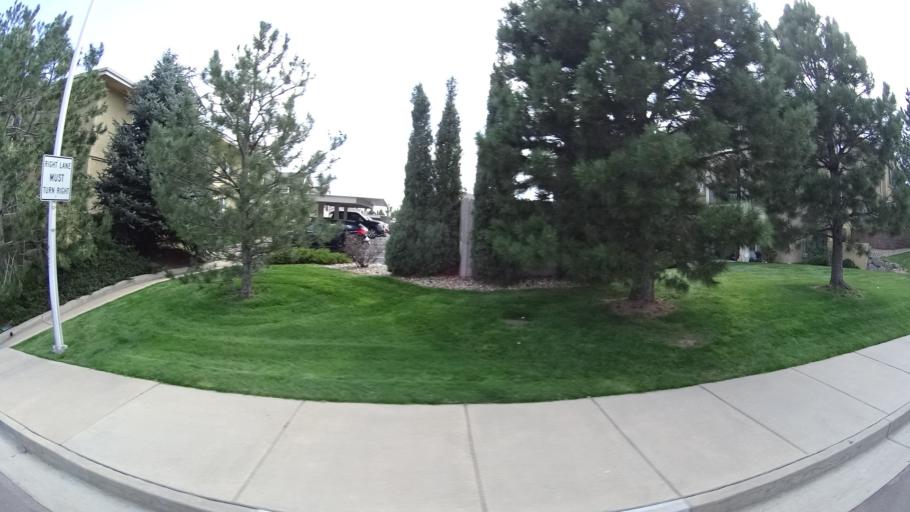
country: US
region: Colorado
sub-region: El Paso County
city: Cimarron Hills
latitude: 38.8771
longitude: -104.7242
